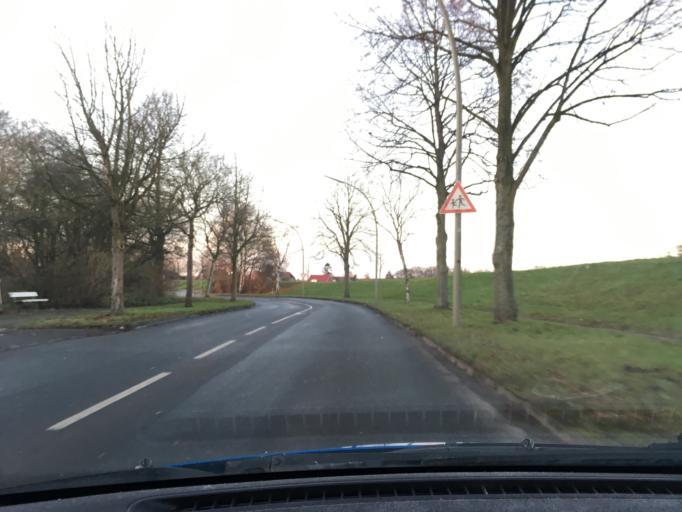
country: DE
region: Hamburg
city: Altona
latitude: 53.5016
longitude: 9.8797
